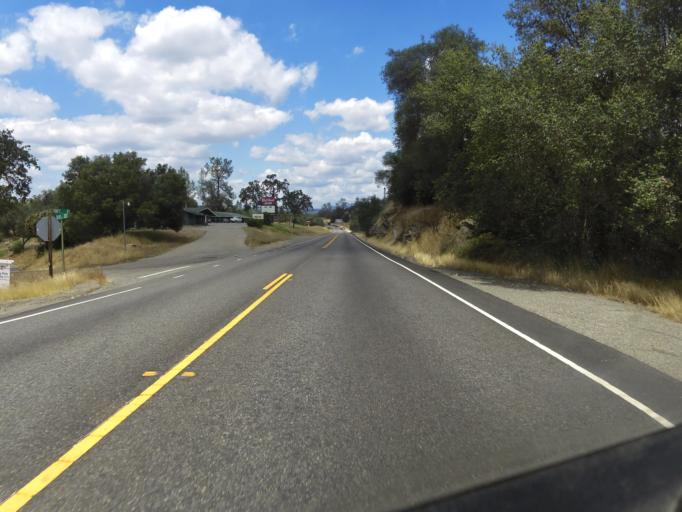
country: US
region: California
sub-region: Madera County
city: Yosemite Lakes
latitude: 37.1488
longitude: -119.7319
